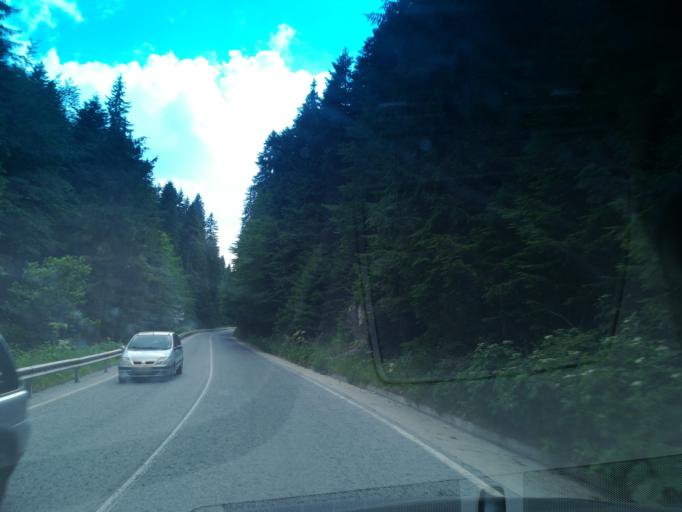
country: BG
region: Smolyan
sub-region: Obshtina Smolyan
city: Smolyan
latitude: 41.6558
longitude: 24.6973
